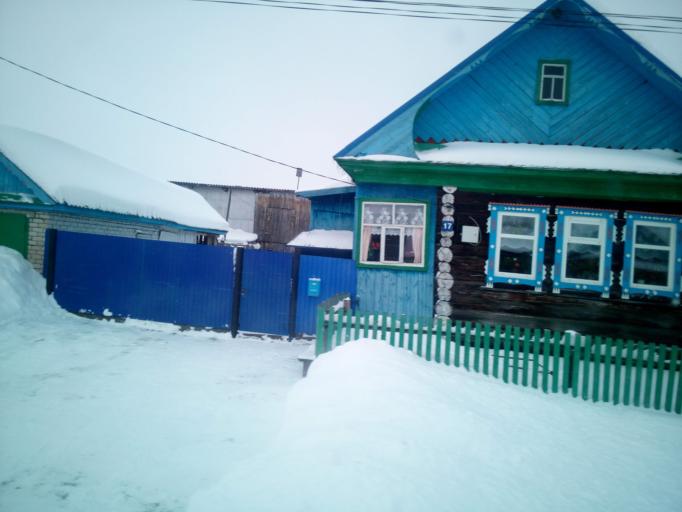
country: RU
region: Bashkortostan
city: Amzya
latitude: 56.1945
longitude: 54.3812
